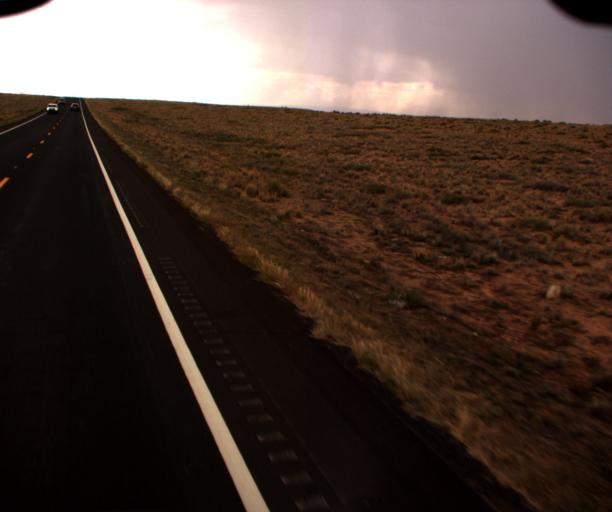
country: US
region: Arizona
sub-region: Coconino County
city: Tuba City
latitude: 36.1869
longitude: -111.0708
